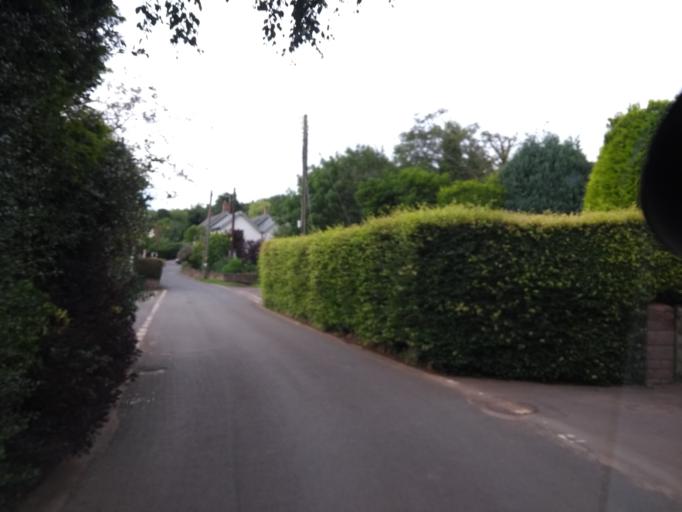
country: GB
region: England
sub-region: Somerset
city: Williton
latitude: 51.1300
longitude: -3.3261
